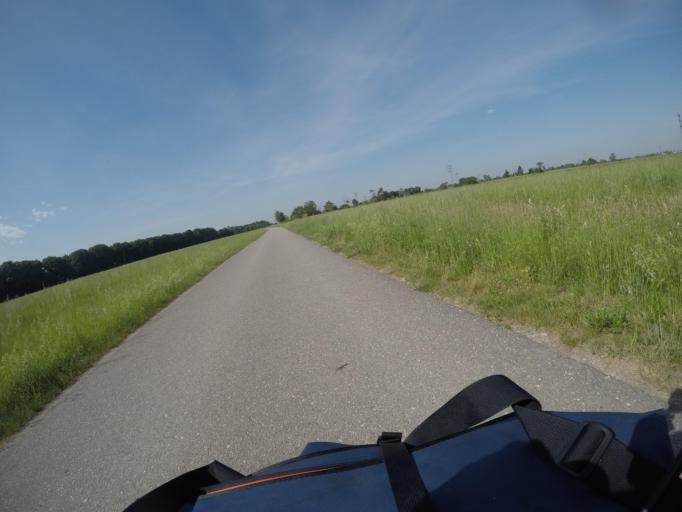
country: DE
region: Baden-Wuerttemberg
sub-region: Karlsruhe Region
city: Bietigheim
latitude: 48.9065
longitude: 8.2813
